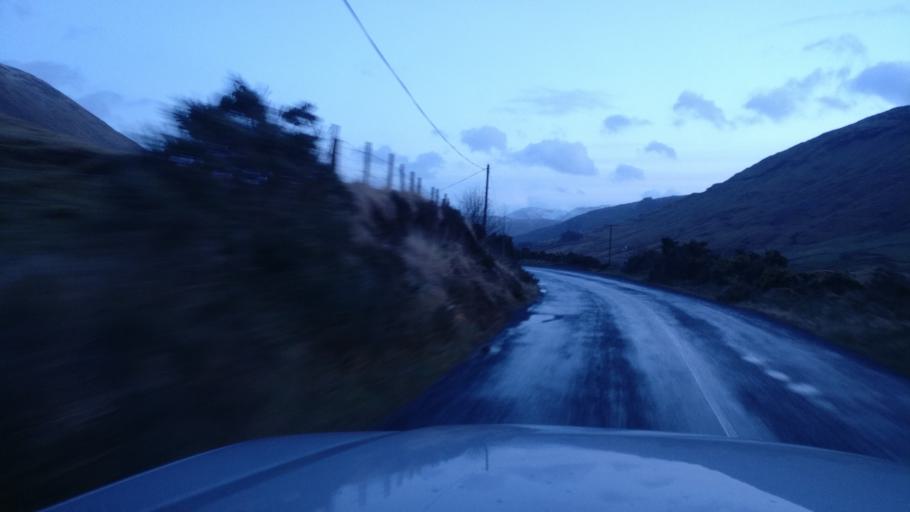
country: IE
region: Connaught
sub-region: Maigh Eo
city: Westport
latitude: 53.5733
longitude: -9.6618
